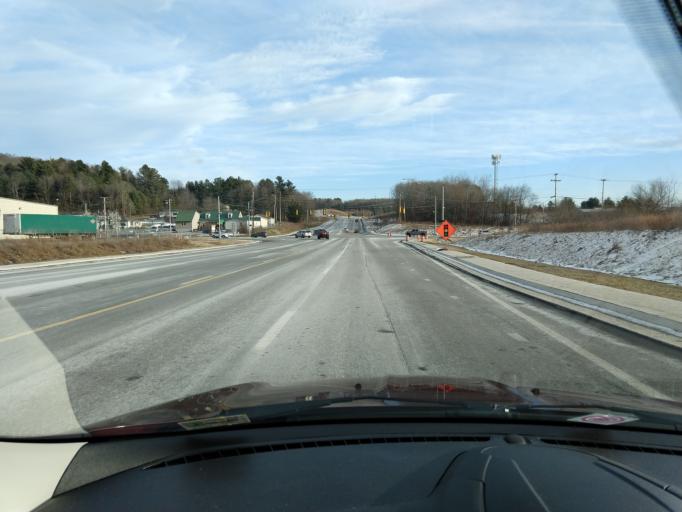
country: US
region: West Virginia
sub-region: Raleigh County
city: Stanaford
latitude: 37.8083
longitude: -81.1804
